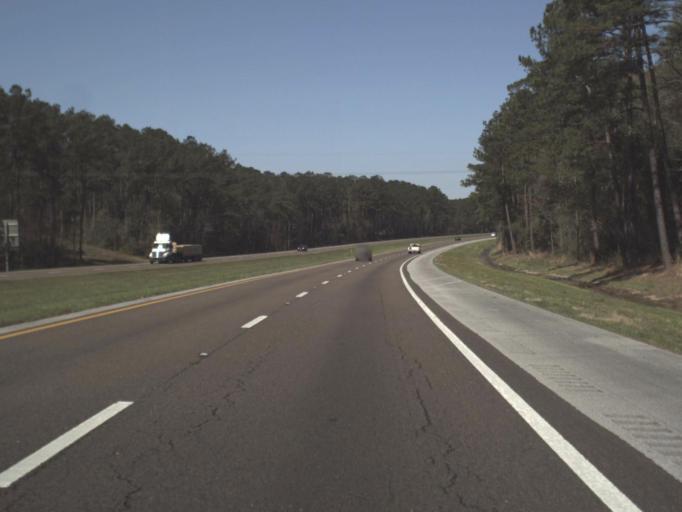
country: US
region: Florida
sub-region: Walton County
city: DeFuniak Springs
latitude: 30.6938
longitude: -86.1418
